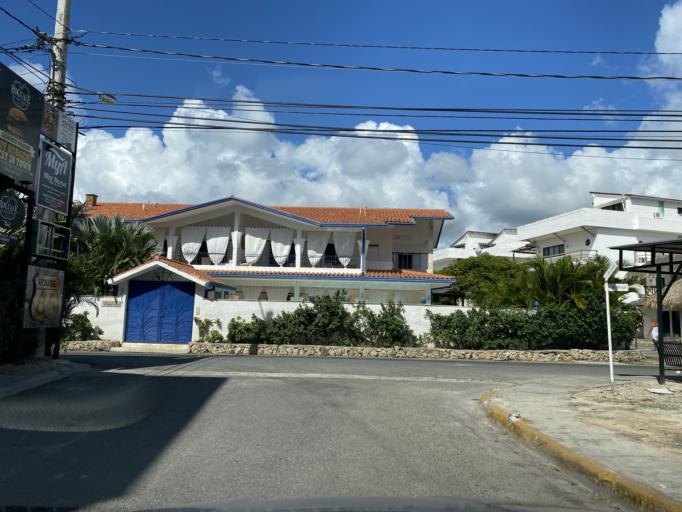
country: DO
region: La Romana
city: La Romana
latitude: 18.3486
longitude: -68.8253
